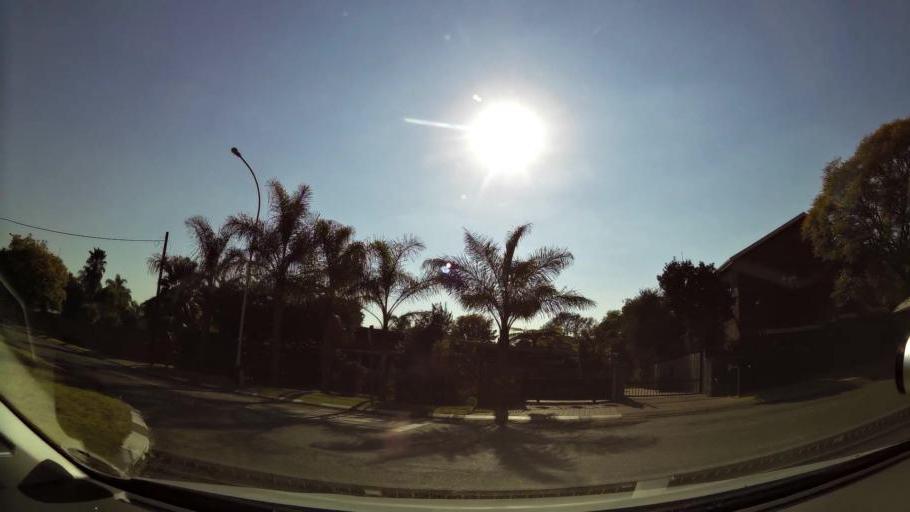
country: ZA
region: Gauteng
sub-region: City of Johannesburg Metropolitan Municipality
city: Modderfontein
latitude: -26.1585
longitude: 28.1371
